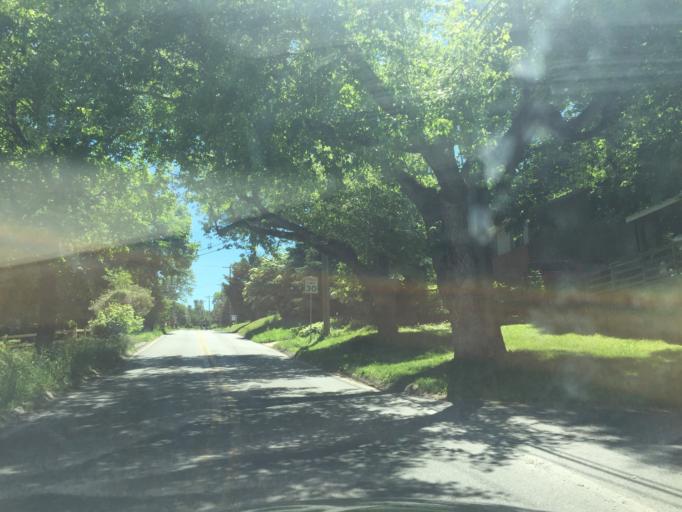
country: US
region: Maryland
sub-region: Carroll County
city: Westminster
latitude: 39.5839
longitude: -76.9745
